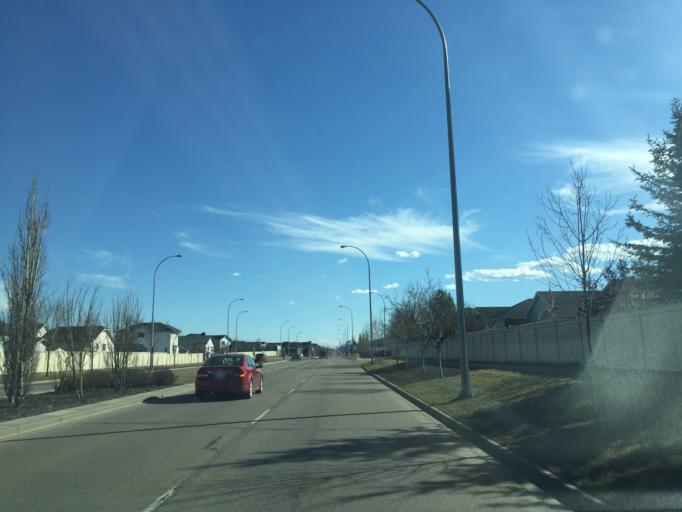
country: CA
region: Alberta
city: Airdrie
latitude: 51.2965
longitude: -114.0254
